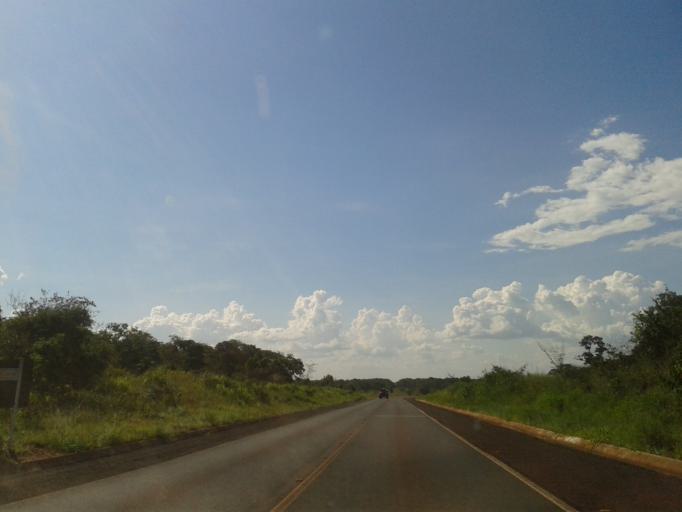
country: BR
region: Minas Gerais
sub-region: Santa Vitoria
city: Santa Vitoria
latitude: -19.0443
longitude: -50.4090
